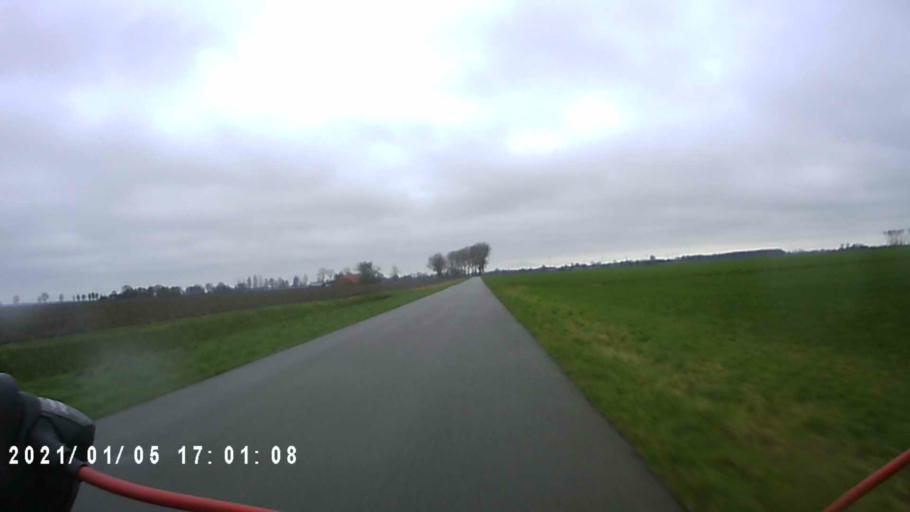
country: NL
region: Groningen
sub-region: Gemeente  Oldambt
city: Winschoten
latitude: 53.2561
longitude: 7.0460
